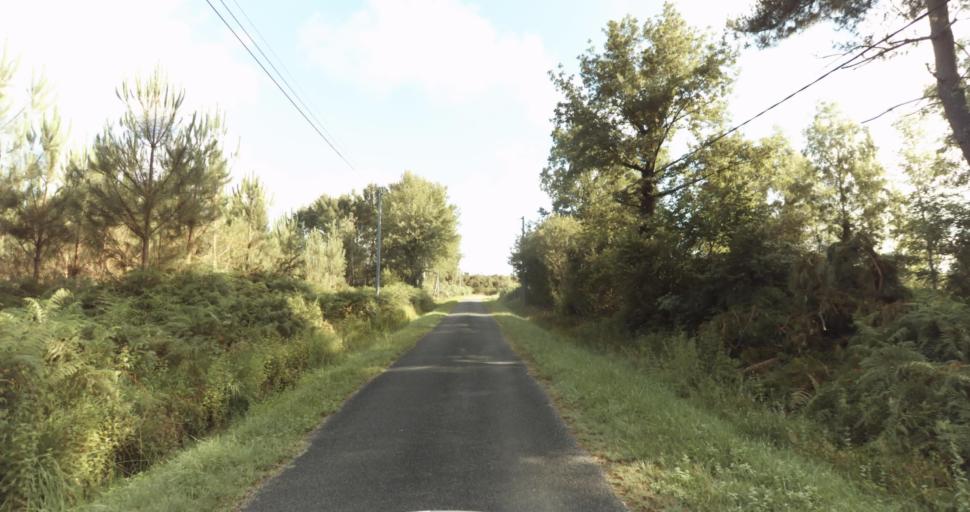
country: FR
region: Aquitaine
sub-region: Departement de la Gironde
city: Bazas
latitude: 44.4437
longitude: -0.2502
